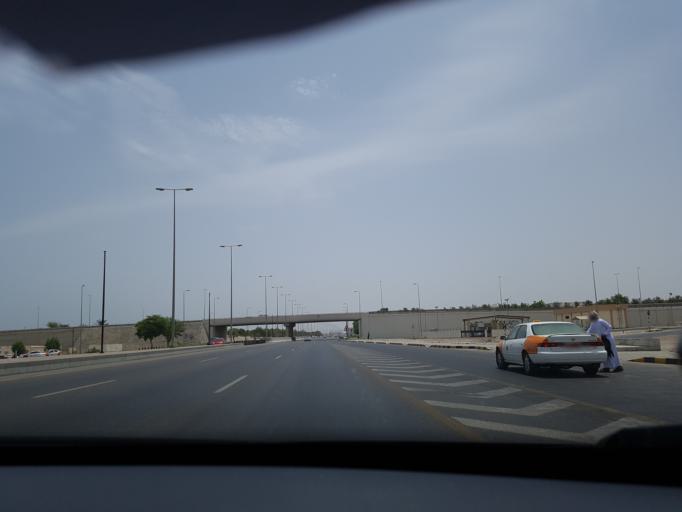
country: OM
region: Muhafazat Masqat
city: As Sib al Jadidah
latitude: 23.6754
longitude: 58.1365
